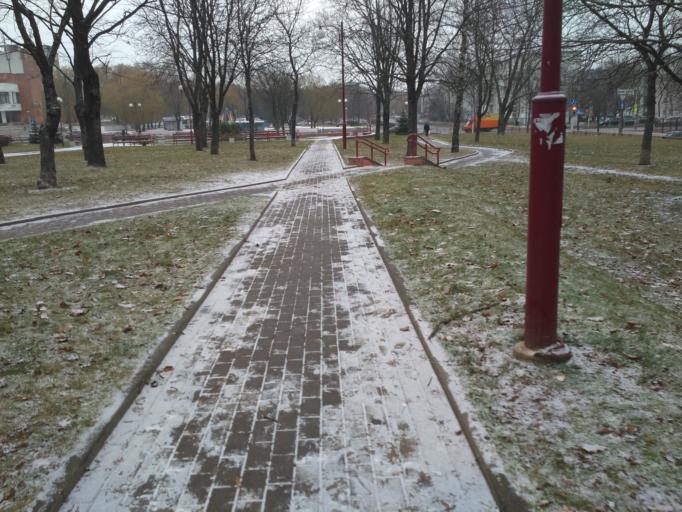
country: BY
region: Minsk
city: Novoye Medvezhino
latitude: 53.9144
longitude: 27.4875
